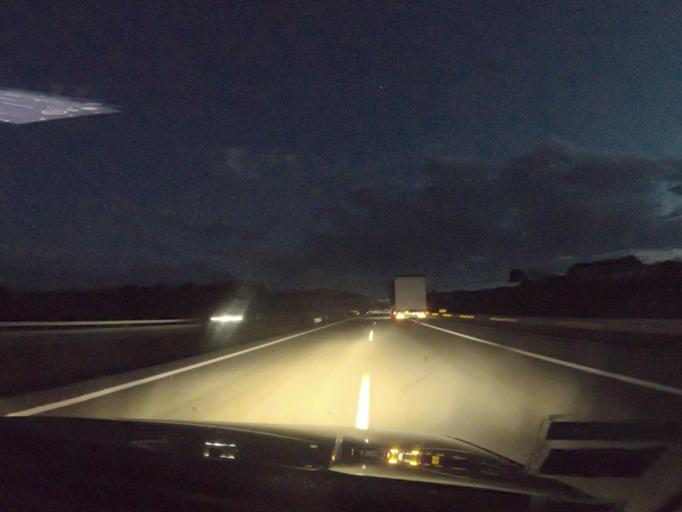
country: ES
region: Castille and Leon
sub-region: Provincia de Leon
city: Brazuelo
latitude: 42.5106
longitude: -6.1167
